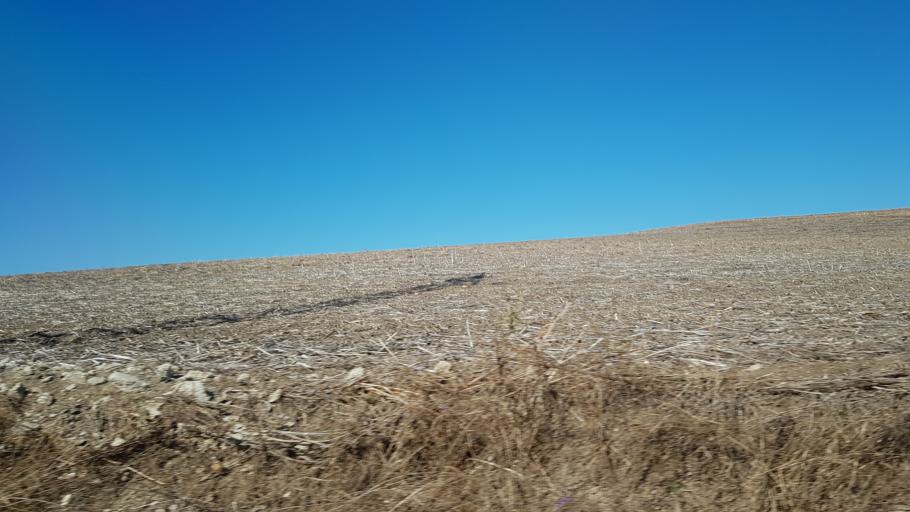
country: TR
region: Tekirdag
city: Corlu
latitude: 41.0327
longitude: 27.8146
